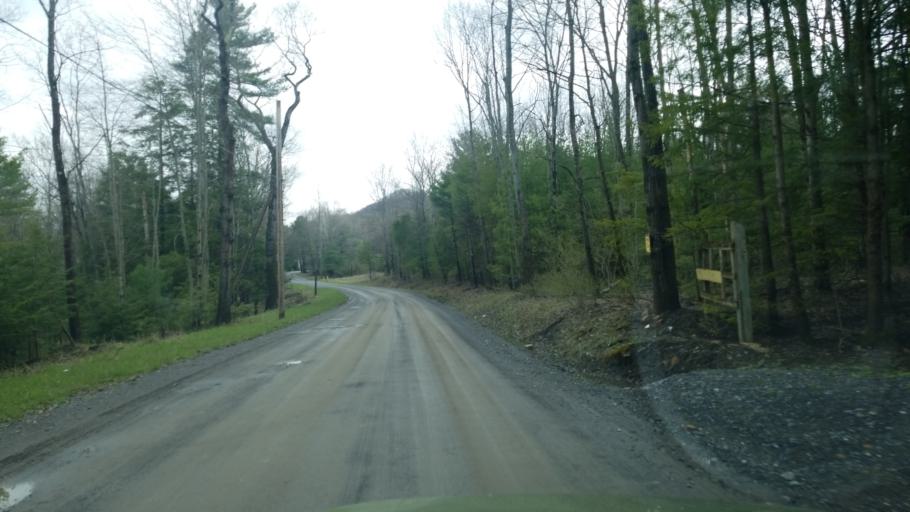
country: US
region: Pennsylvania
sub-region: Clearfield County
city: Shiloh
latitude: 41.1210
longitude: -78.3407
